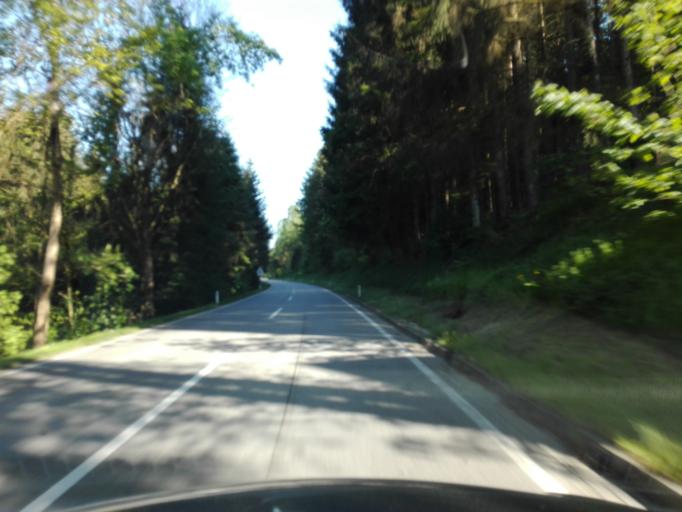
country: AT
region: Upper Austria
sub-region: Politischer Bezirk Rohrbach
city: Pfarrkirchen im Muehlkreis
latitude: 48.4871
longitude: 13.7476
